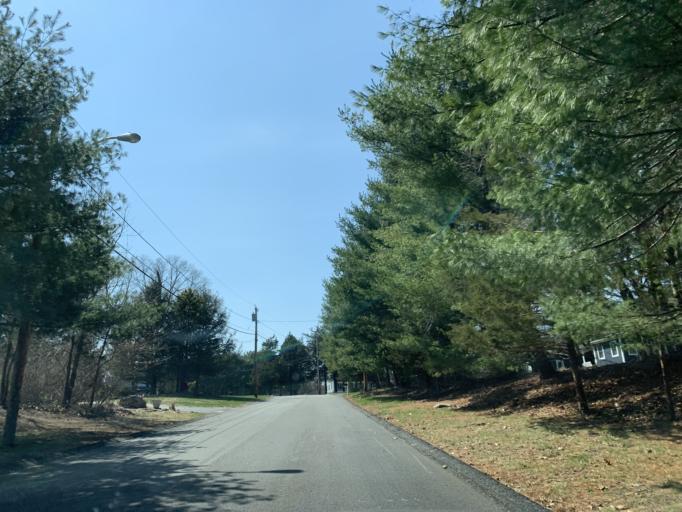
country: US
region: Rhode Island
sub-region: Kent County
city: East Greenwich
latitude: 41.6317
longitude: -71.4330
